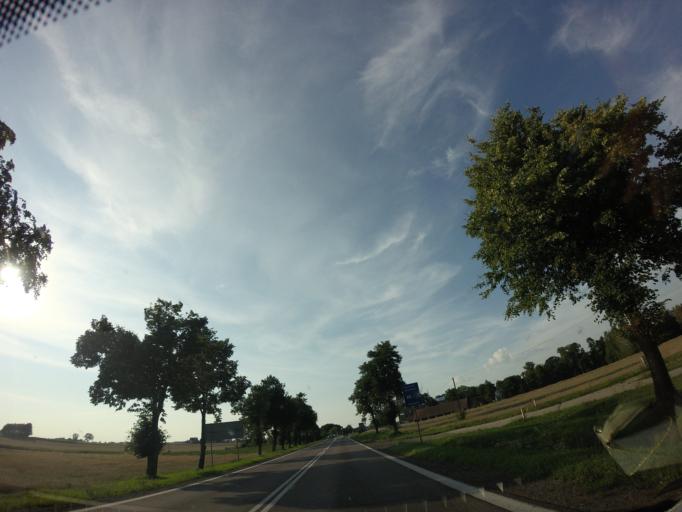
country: PL
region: Podlasie
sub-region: Powiat sokolski
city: Janow
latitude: 53.4380
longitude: 23.0972
